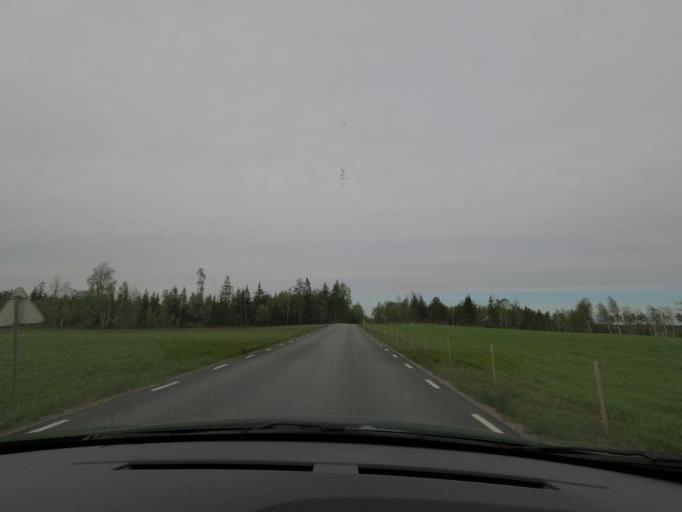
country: SE
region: Joenkoeping
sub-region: Varnamo Kommun
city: Bredaryd
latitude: 57.1482
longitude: 13.7257
